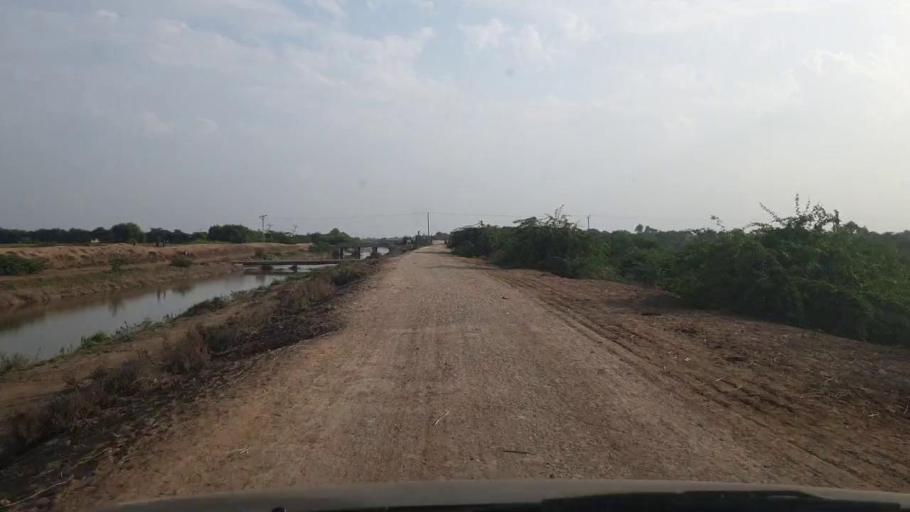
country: PK
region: Sindh
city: Badin
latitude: 24.5514
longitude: 68.6706
